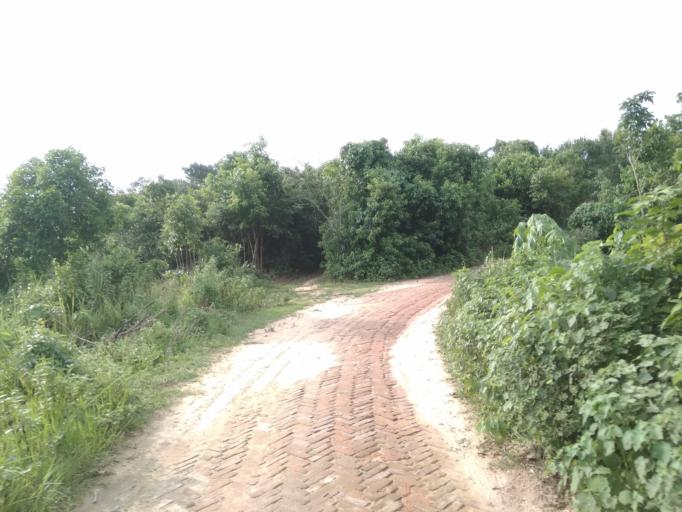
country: BD
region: Chittagong
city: Manikchari
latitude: 22.9276
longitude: 91.9127
